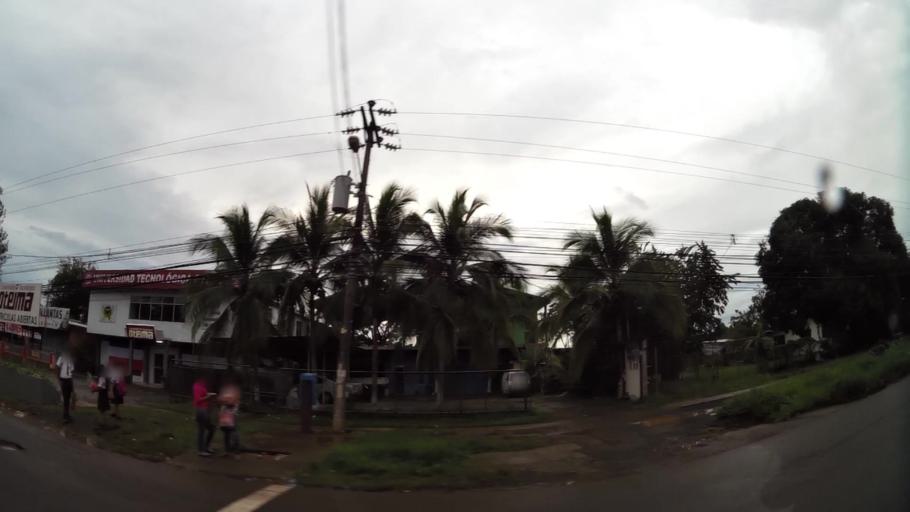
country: PA
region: Veraguas
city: Santiago de Veraguas
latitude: 8.1138
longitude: -80.9689
